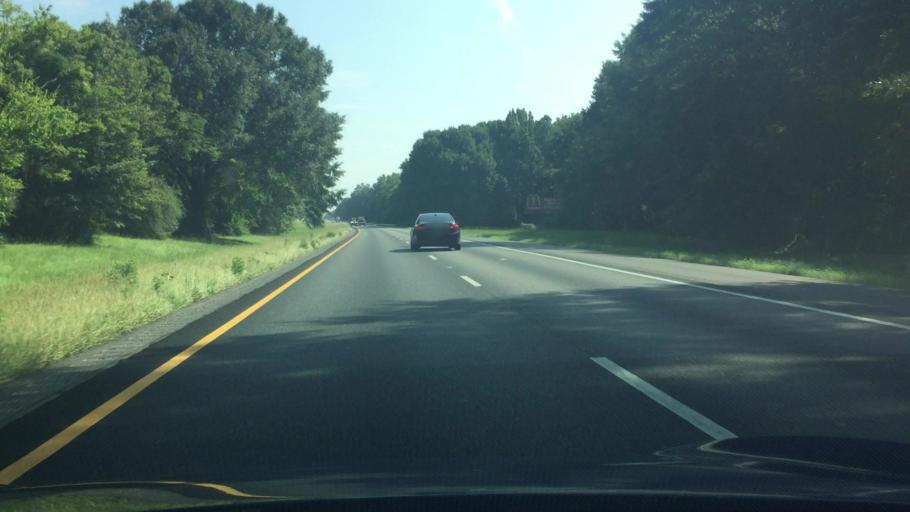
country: US
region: Alabama
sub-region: Montgomery County
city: Montgomery
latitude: 32.2338
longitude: -86.3815
